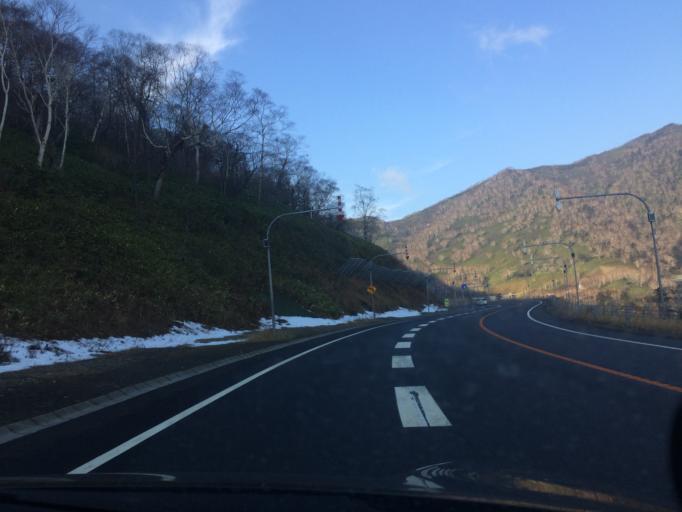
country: JP
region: Hokkaido
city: Otofuke
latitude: 42.9593
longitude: 142.7722
